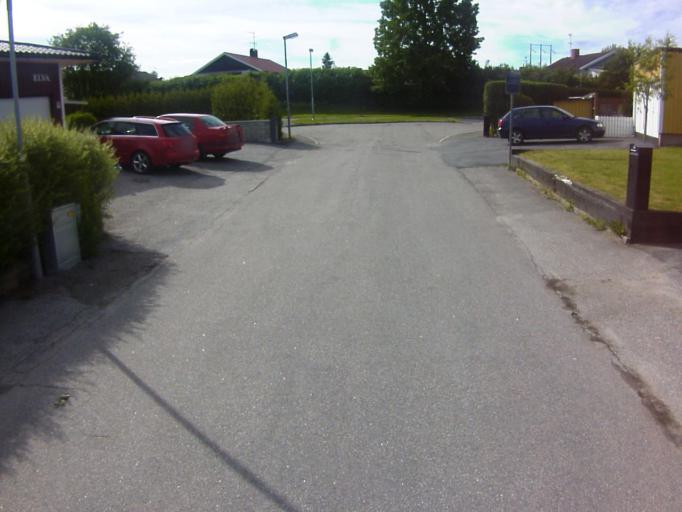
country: SE
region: Soedermanland
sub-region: Eskilstuna Kommun
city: Skogstorp
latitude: 59.3516
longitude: 16.4500
